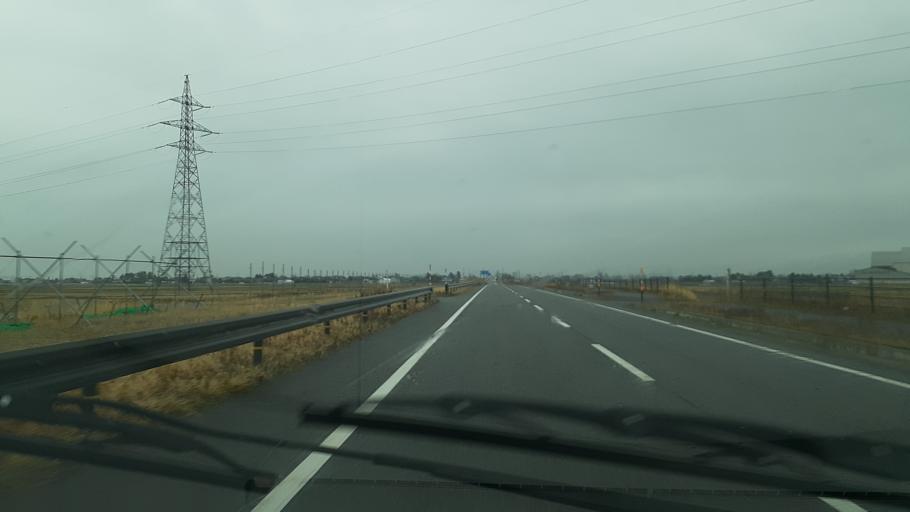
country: JP
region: Niigata
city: Kameda-honcho
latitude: 37.8716
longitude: 139.1504
